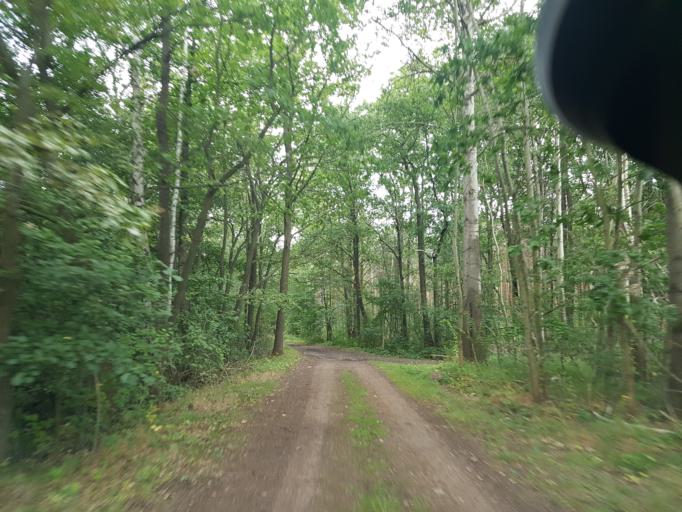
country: DE
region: Brandenburg
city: Ruckersdorf
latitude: 51.5991
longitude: 13.5702
